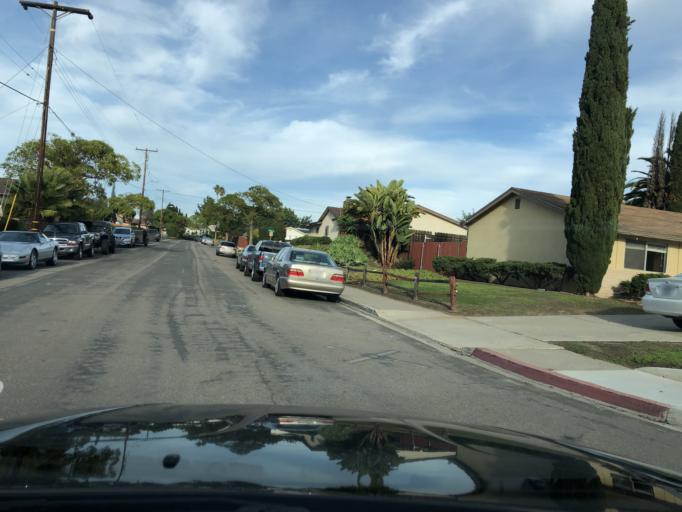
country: US
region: California
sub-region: San Diego County
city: La Jolla
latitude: 32.8238
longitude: -117.1775
